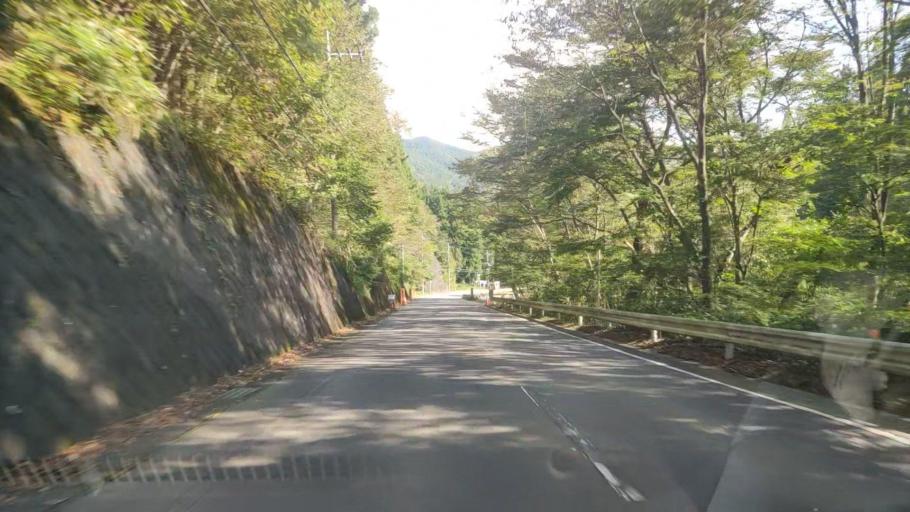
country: JP
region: Gunma
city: Nakanojomachi
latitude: 36.6137
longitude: 138.7405
